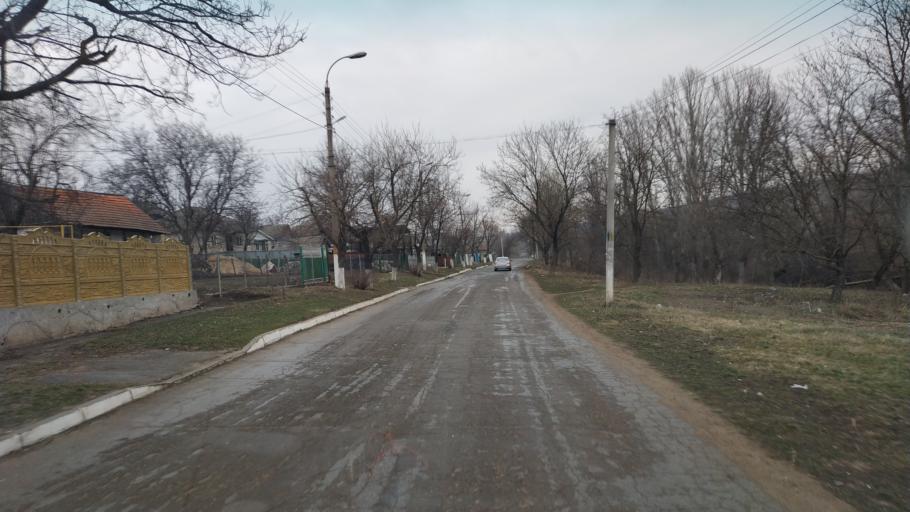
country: MD
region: Chisinau
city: Singera
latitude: 46.8345
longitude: 28.9781
